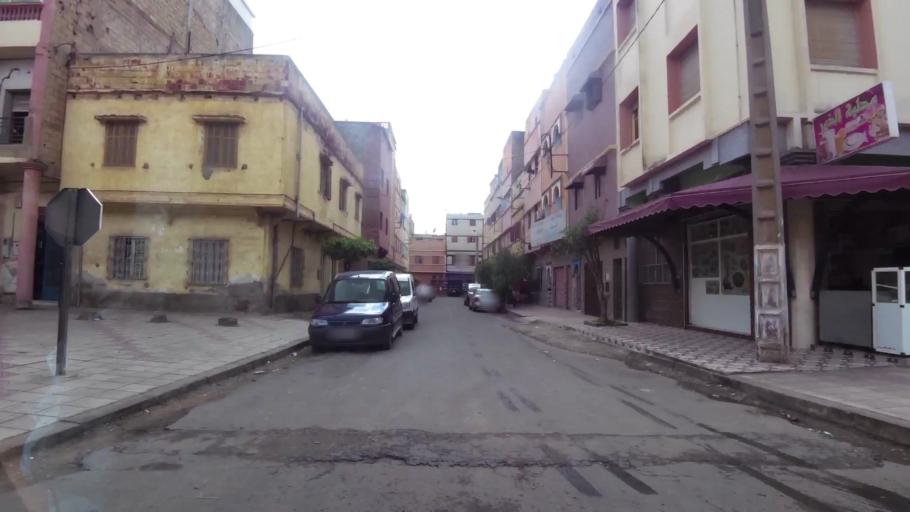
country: MA
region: Chaouia-Ouardigha
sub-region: Settat Province
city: Berrechid
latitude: 33.2729
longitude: -7.5869
